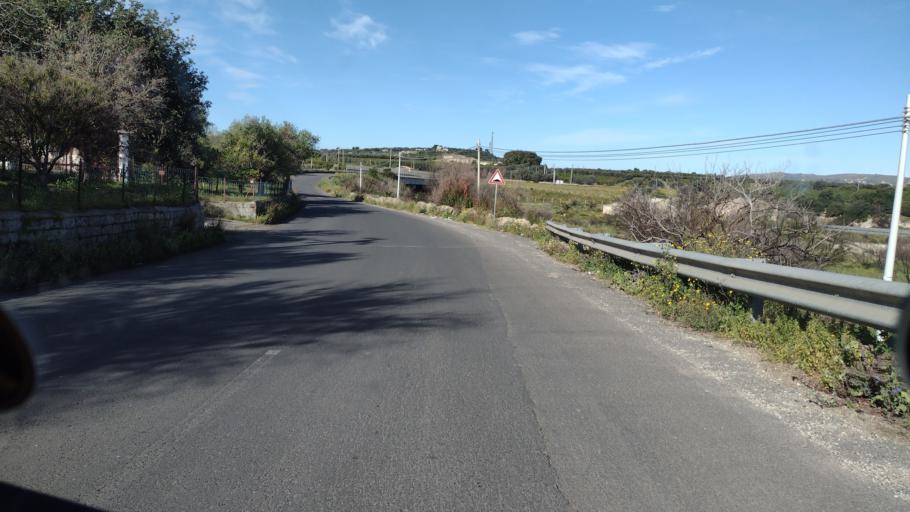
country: IT
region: Sicily
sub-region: Provincia di Siracusa
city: Noto
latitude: 36.8761
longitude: 15.1081
